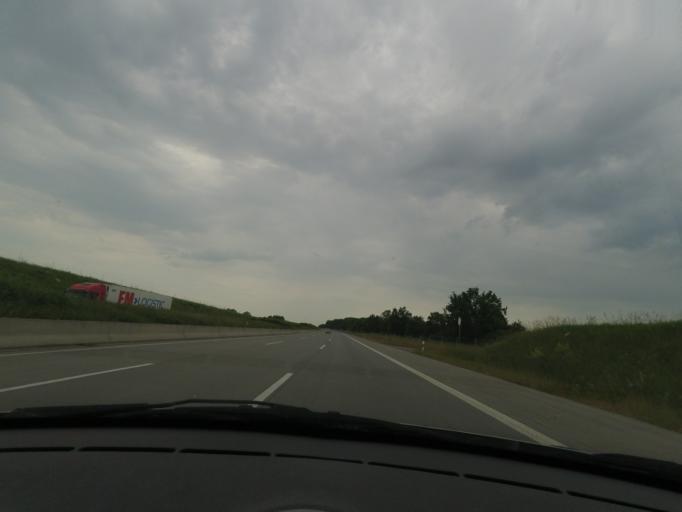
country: DE
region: Thuringia
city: Posterstein
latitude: 50.8681
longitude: 12.2659
